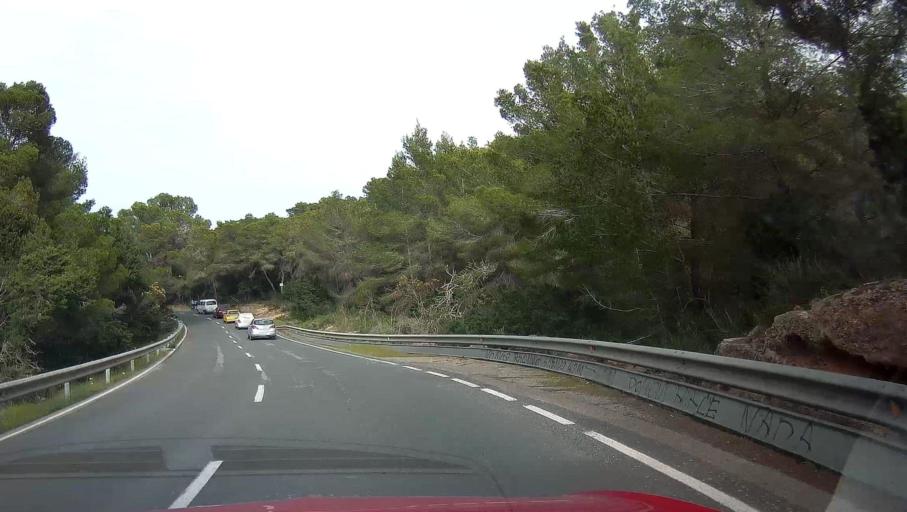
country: ES
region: Balearic Islands
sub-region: Illes Balears
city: Sant Joan de Labritja
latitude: 39.0994
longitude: 1.5055
